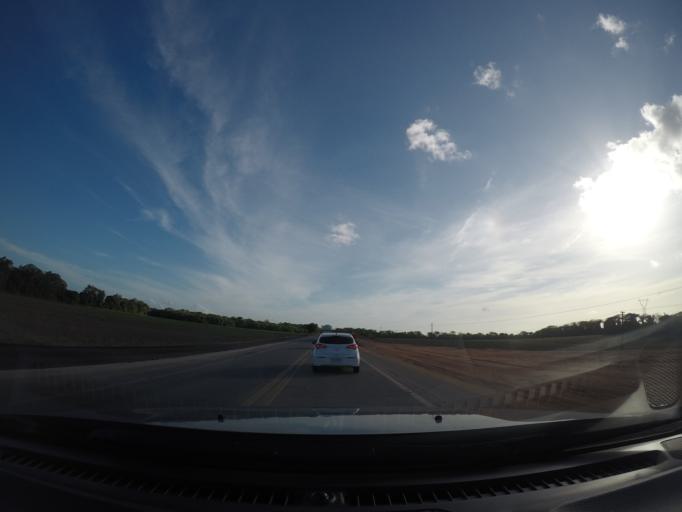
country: BR
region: Alagoas
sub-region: Pilar
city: Pilar
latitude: -9.6067
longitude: -36.0266
